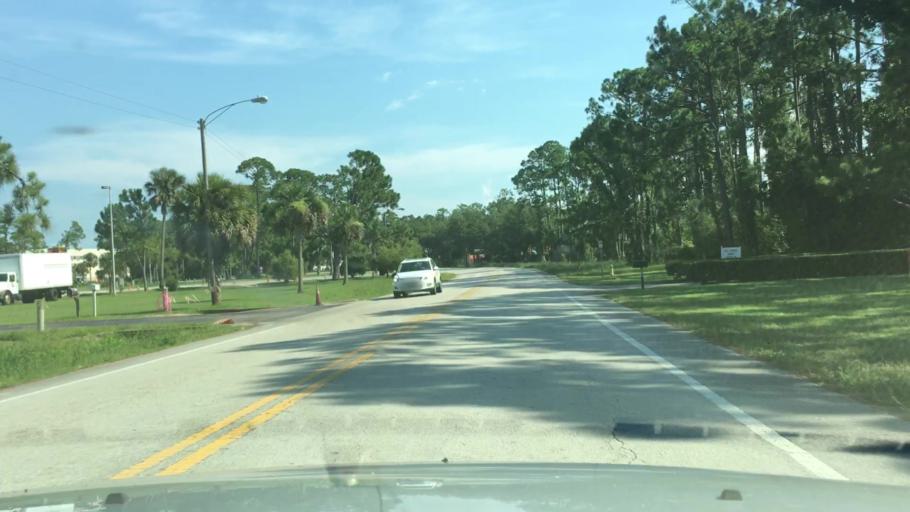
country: US
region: Florida
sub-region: Volusia County
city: Daytona Beach
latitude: 29.1917
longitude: -81.0793
